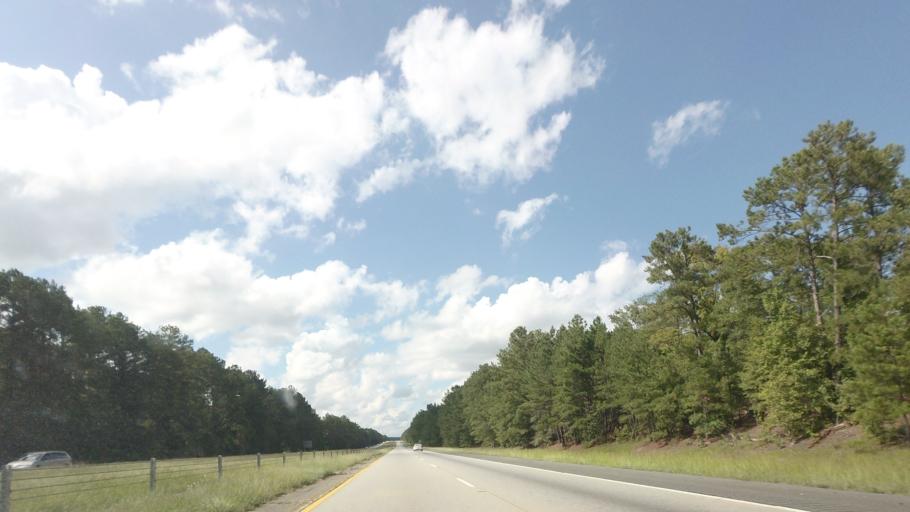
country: US
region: Georgia
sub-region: Houston County
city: Warner Robins
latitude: 32.7341
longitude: -83.5397
